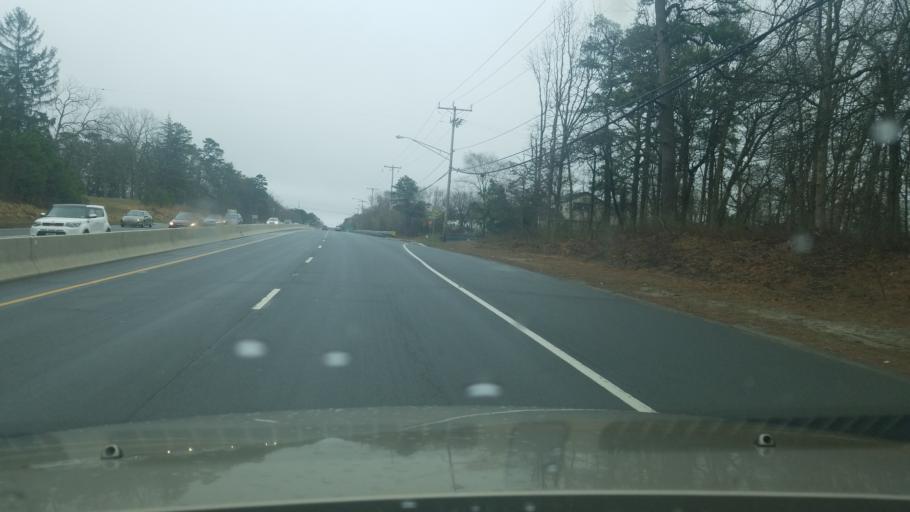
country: US
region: New Jersey
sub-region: Ocean County
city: Leisure Knoll
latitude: 40.0041
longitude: -74.2953
